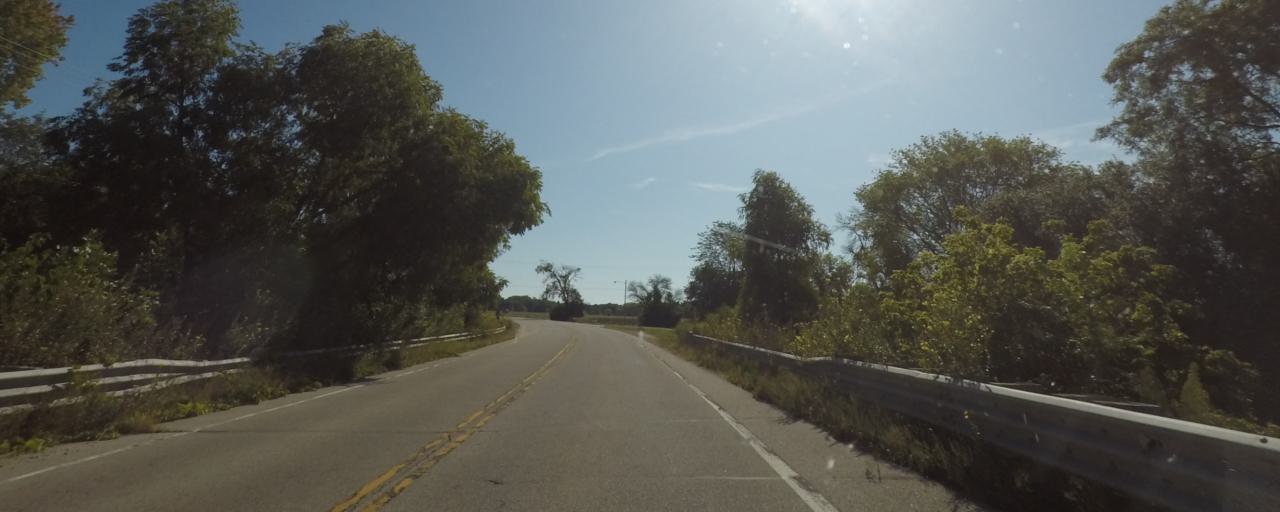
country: US
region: Wisconsin
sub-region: Waukesha County
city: Dousman
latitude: 43.0213
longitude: -88.4961
